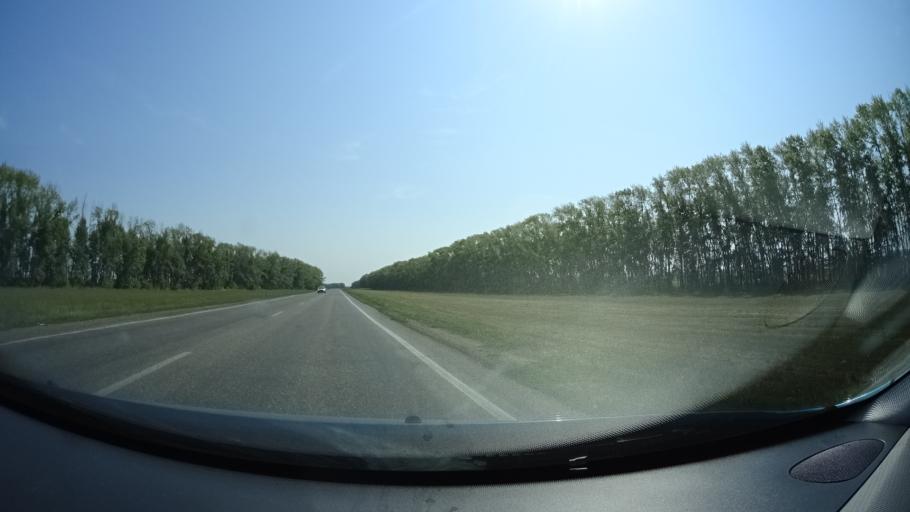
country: RU
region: Bashkortostan
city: Karmaskaly
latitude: 54.3920
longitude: 56.1192
